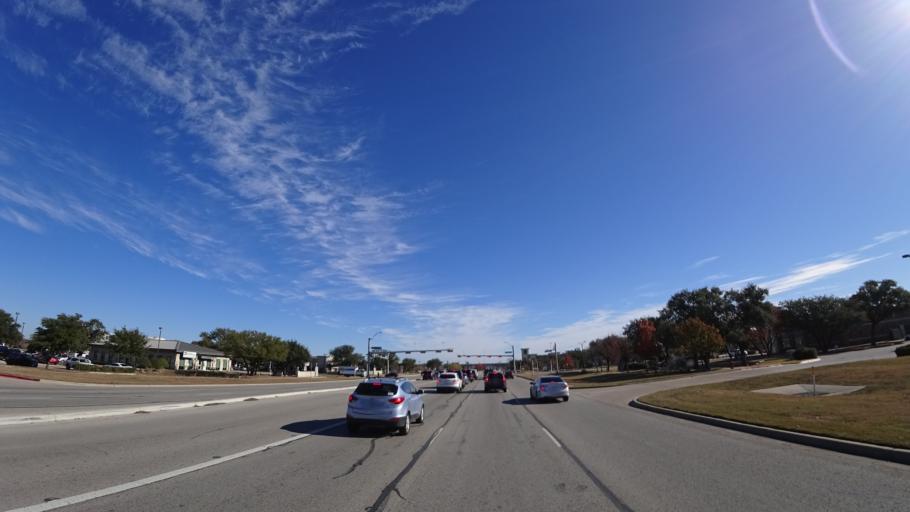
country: US
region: Texas
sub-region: Williamson County
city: Cedar Park
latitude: 30.5235
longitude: -97.8218
